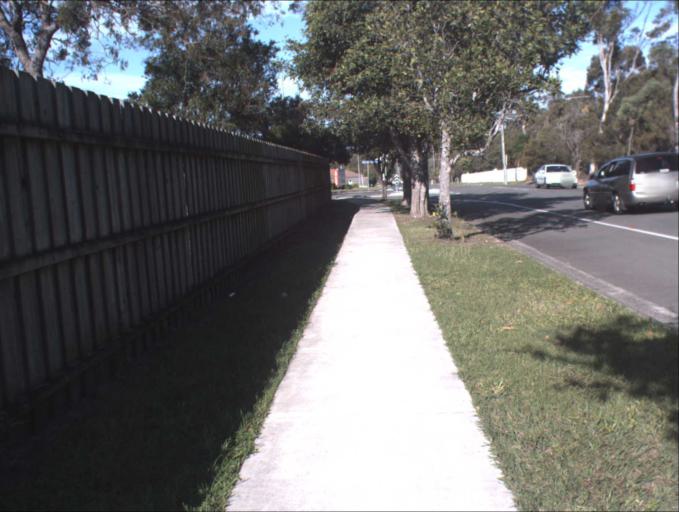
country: AU
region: Queensland
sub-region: Logan
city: Logan Reserve
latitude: -27.6973
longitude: 153.0811
